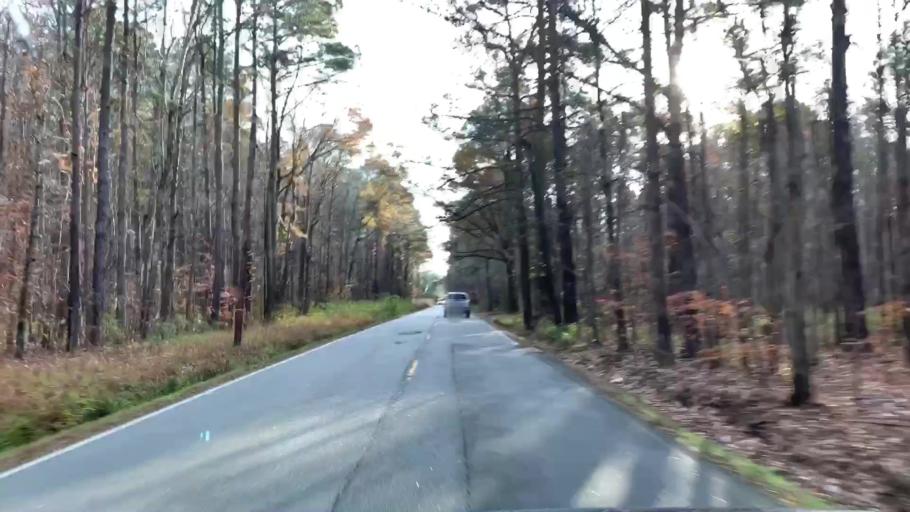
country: US
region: Virginia
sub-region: City of Virginia Beach
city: Virginia Beach
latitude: 36.7396
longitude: -76.1086
